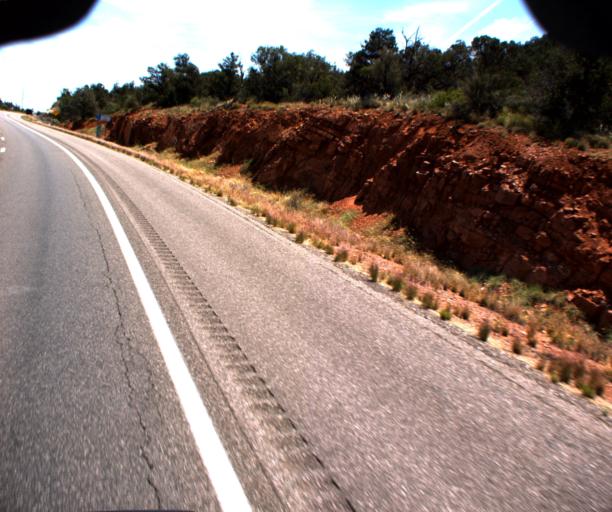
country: US
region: Arizona
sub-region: Yavapai County
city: West Sedona
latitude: 34.8458
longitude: -111.8395
